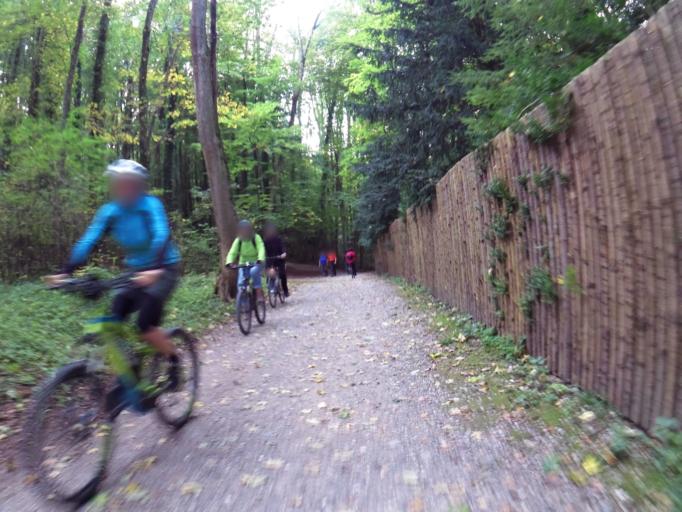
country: DE
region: Bavaria
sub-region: Upper Bavaria
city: Berg
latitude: 47.9677
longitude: 11.3515
